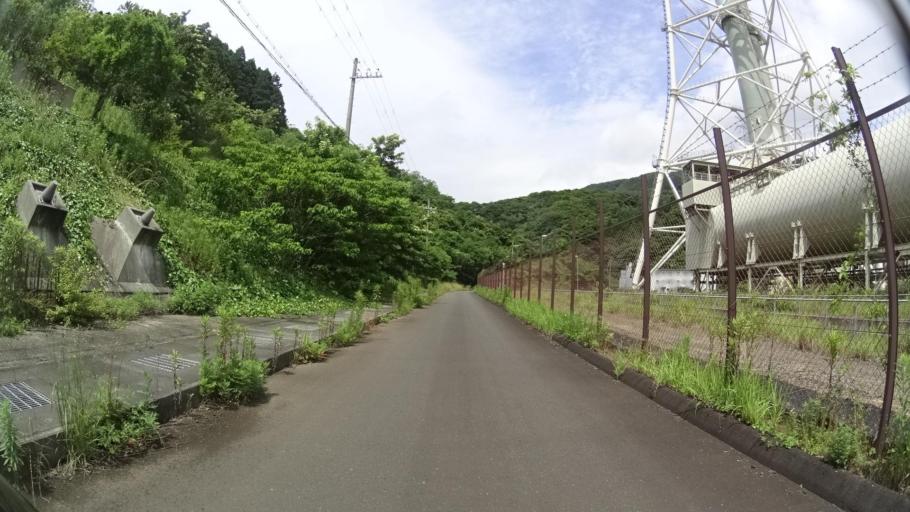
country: JP
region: Kyoto
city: Maizuru
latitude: 35.5317
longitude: 135.3444
